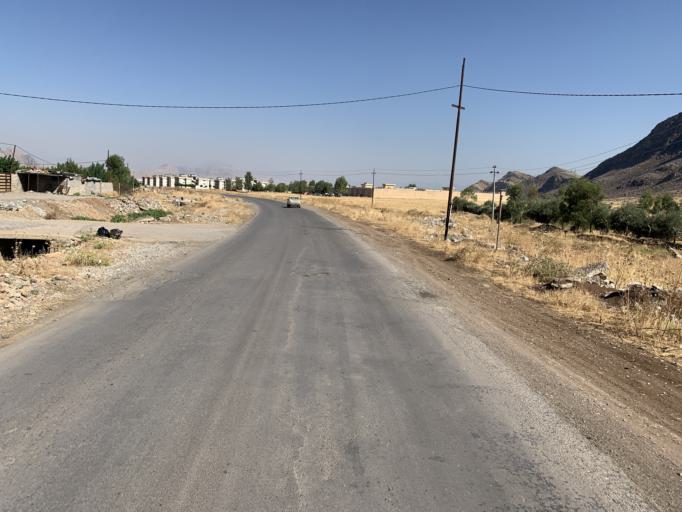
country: IQ
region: As Sulaymaniyah
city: Raniye
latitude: 36.2668
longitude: 44.8396
